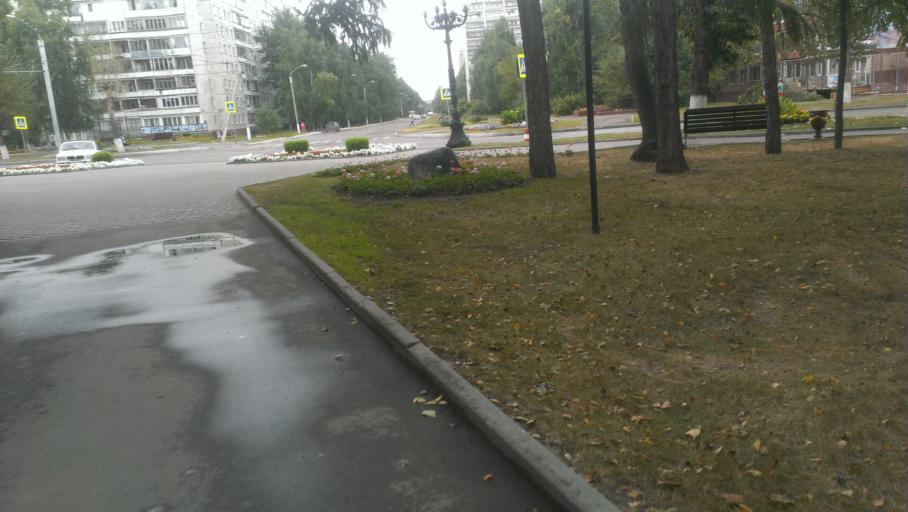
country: RU
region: Altai Krai
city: Novosilikatnyy
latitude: 53.3735
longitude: 83.6699
